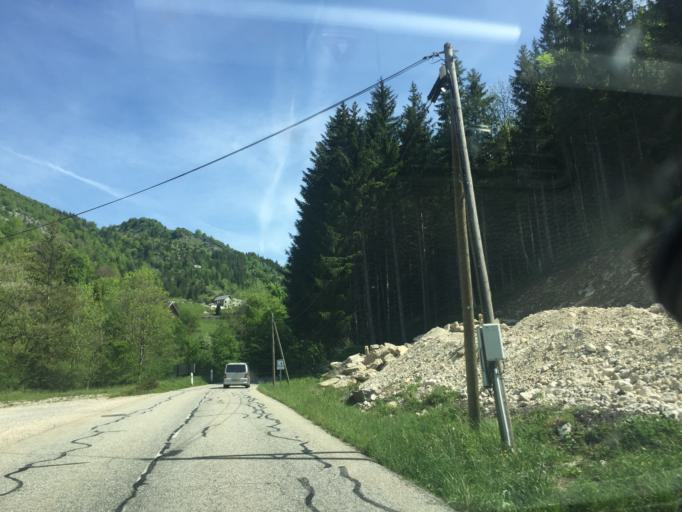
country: FR
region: Rhone-Alpes
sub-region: Departement de l'Isere
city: Saint-Vincent-de-Mercuze
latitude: 45.4223
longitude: 5.8615
